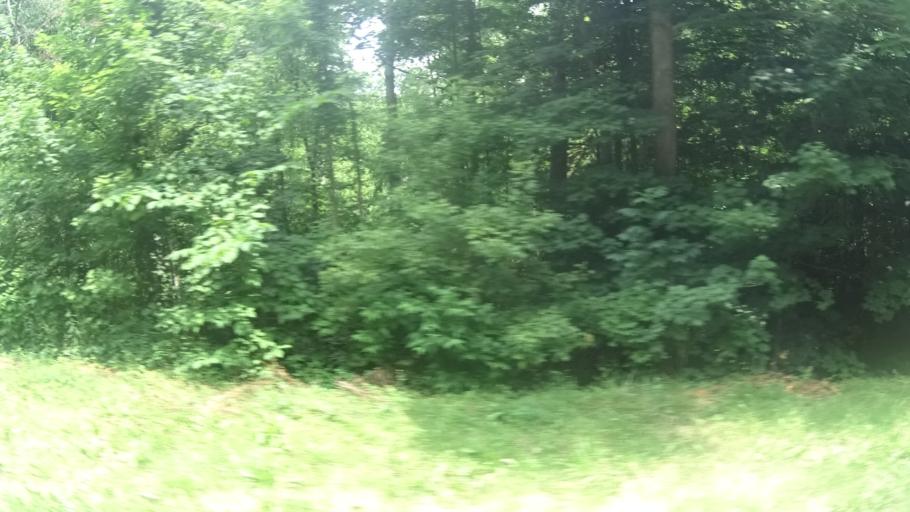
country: US
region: Ohio
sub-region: Erie County
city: Milan
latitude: 41.2878
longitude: -82.6433
